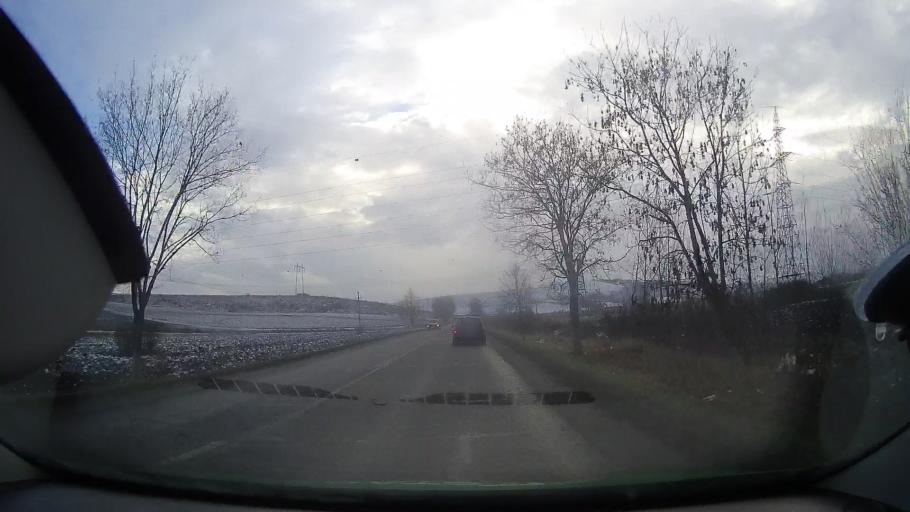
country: RO
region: Mures
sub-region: Comuna Cucerdea
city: Cucerdea
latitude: 46.4233
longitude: 24.2595
